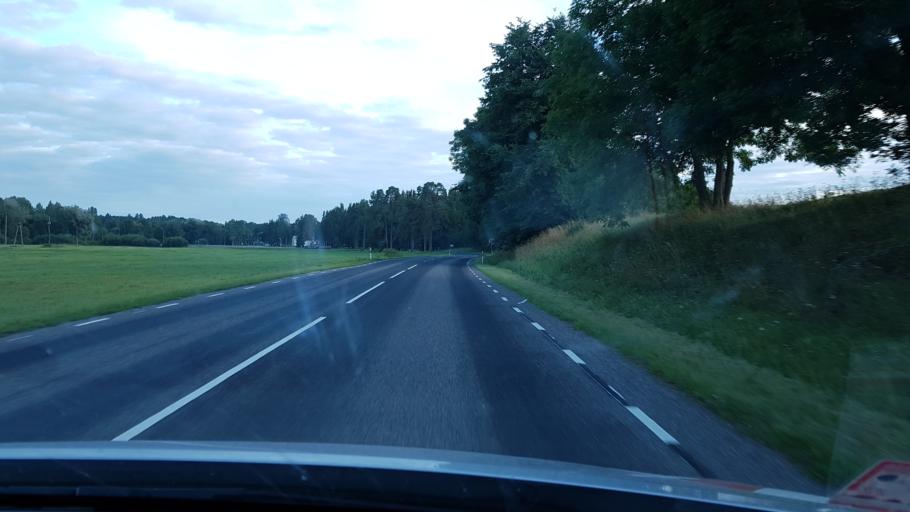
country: EE
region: Vorumaa
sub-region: Voru linn
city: Voru
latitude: 57.8574
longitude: 26.8277
